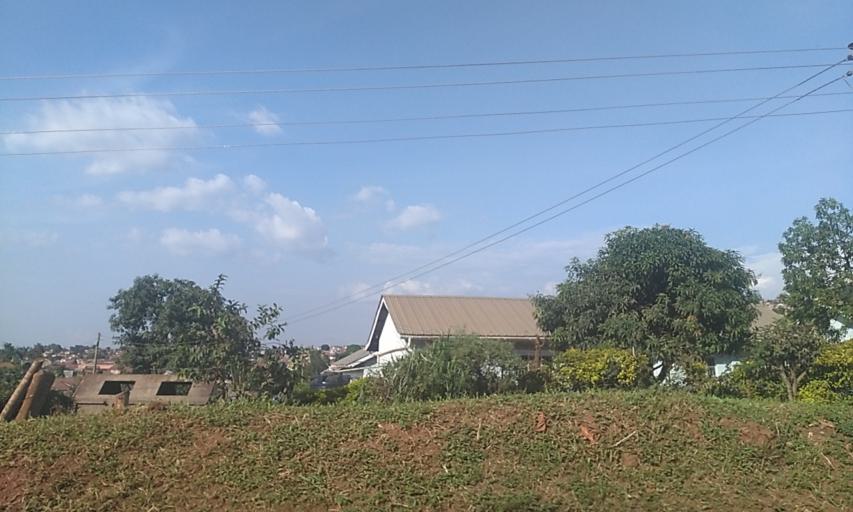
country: UG
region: Central Region
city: Kampala Central Division
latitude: 0.3262
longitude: 32.5376
